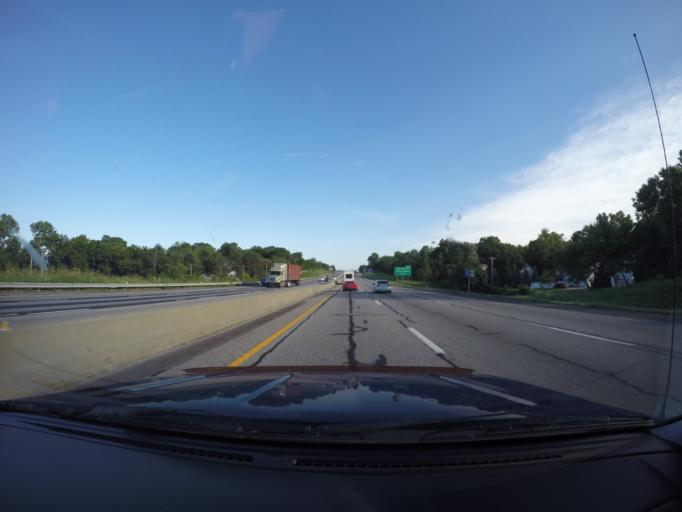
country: US
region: Missouri
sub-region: Platte County
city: Parkville
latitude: 39.2147
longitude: -94.6423
